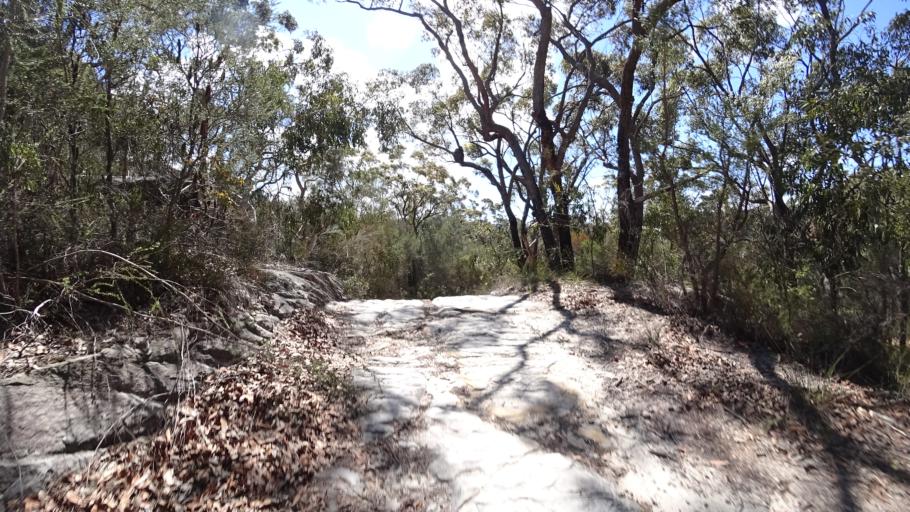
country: AU
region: New South Wales
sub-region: Warringah
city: Killarney Heights
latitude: -33.7640
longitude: 151.2219
